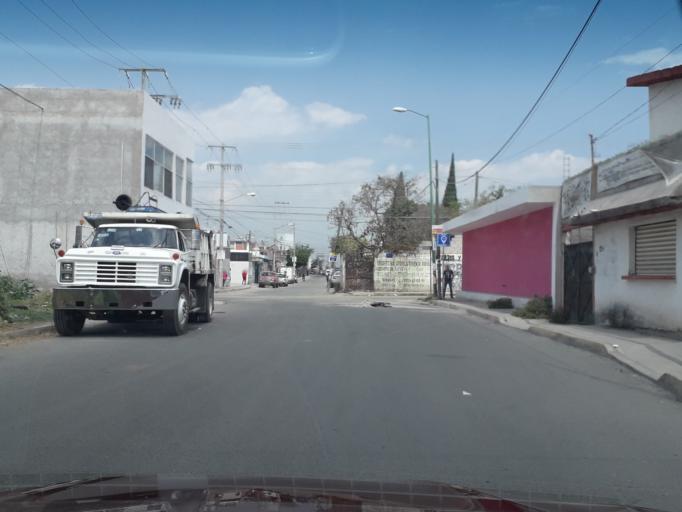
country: MX
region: Puebla
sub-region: Puebla
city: El Capulo (La Quebradora)
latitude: 18.9689
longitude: -98.2598
